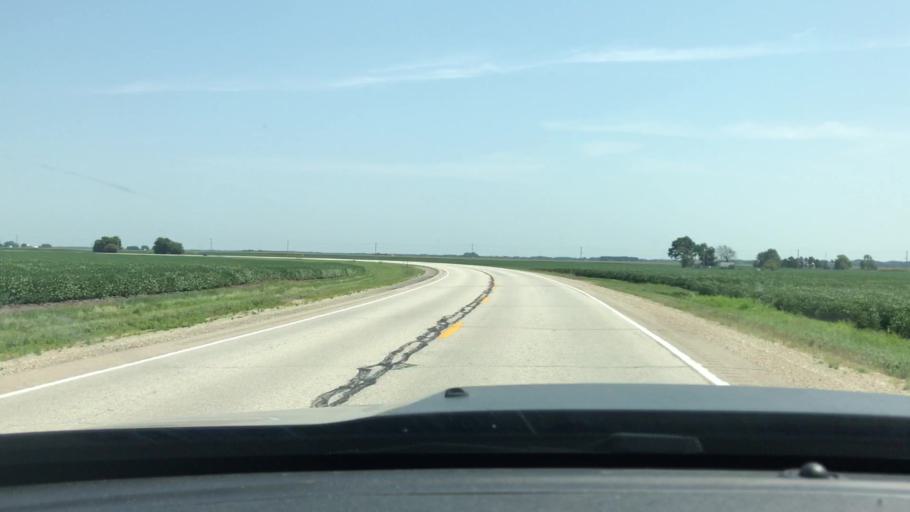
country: US
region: Illinois
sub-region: LaSalle County
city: Ottawa
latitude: 41.4711
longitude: -88.8212
